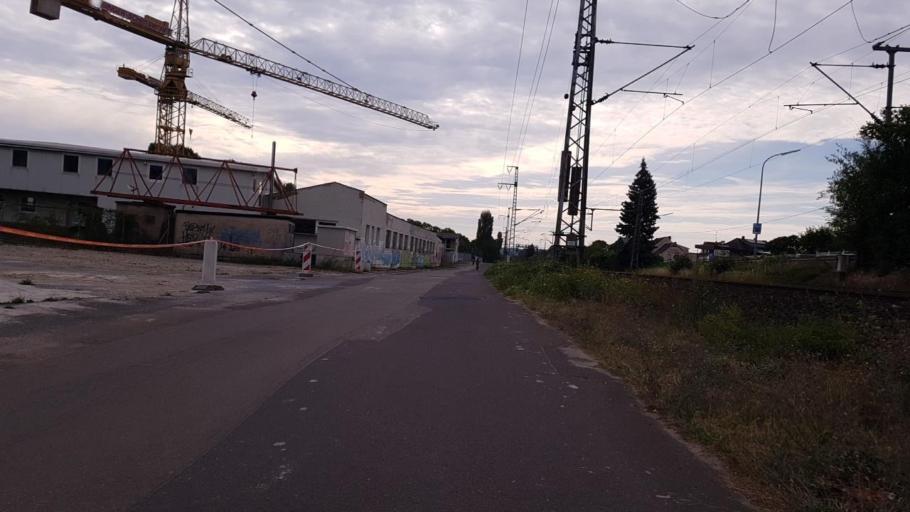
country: DE
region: Hesse
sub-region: Regierungsbezirk Darmstadt
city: Rudesheim am Rhein
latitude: 49.9698
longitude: 7.9324
